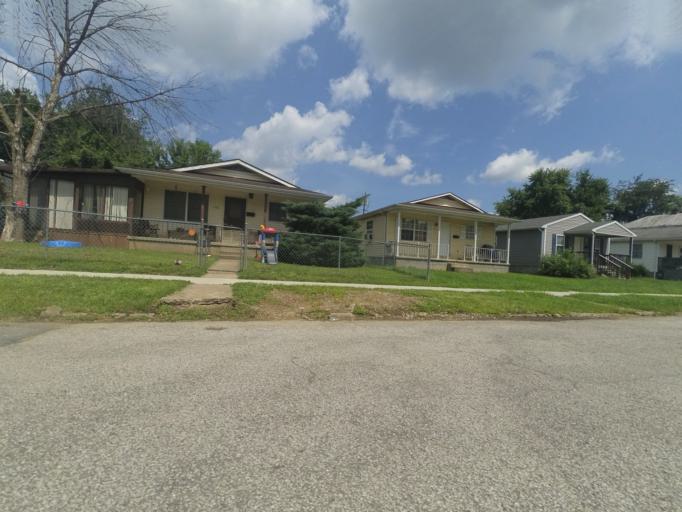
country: US
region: West Virginia
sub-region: Cabell County
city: Huntington
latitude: 38.4157
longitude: -82.4254
